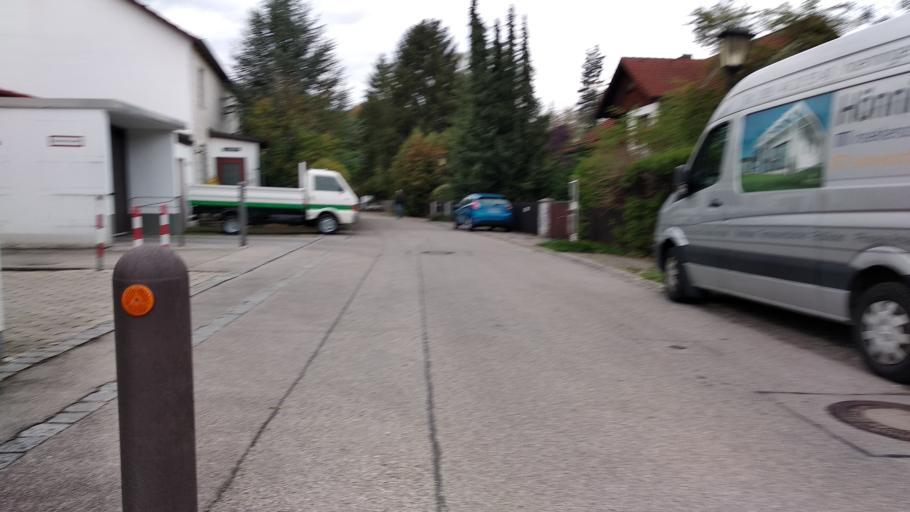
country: DE
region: Bavaria
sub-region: Upper Bavaria
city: Putzbrunn
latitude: 48.0771
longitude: 11.7178
